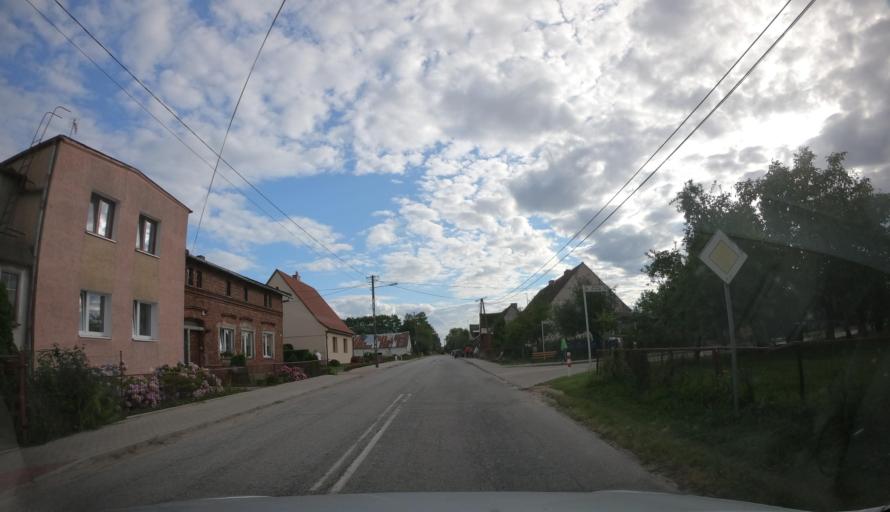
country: PL
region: West Pomeranian Voivodeship
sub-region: Powiat slawienski
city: Slawno
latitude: 54.3245
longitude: 16.6898
